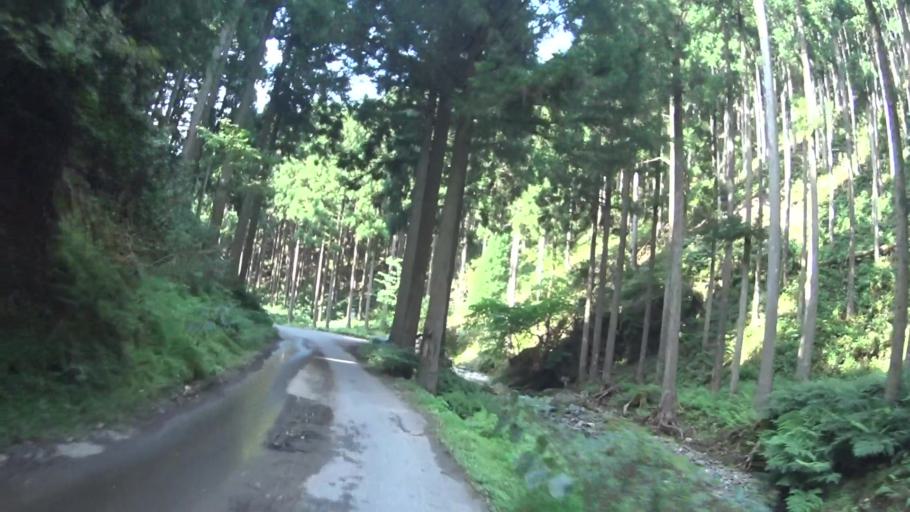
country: JP
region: Fukui
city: Obama
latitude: 35.2670
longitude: 135.6439
